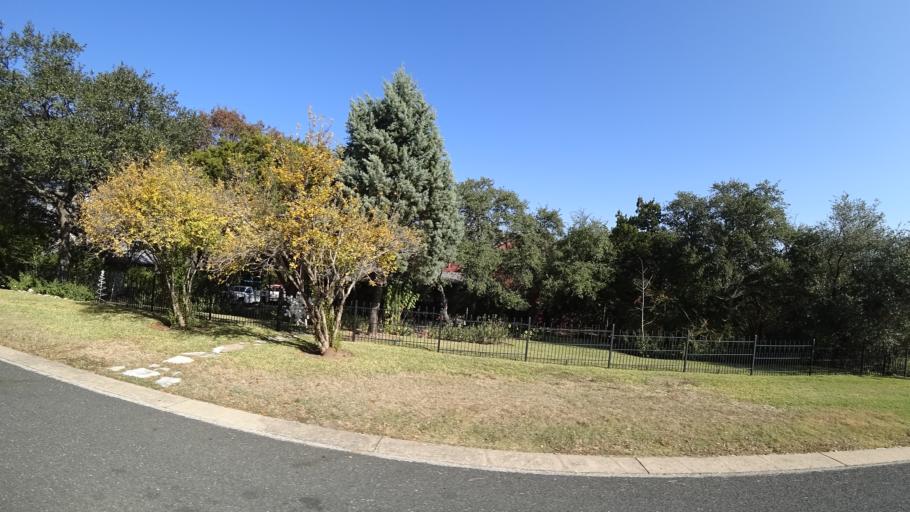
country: US
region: Texas
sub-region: Travis County
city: West Lake Hills
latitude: 30.3728
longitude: -97.8229
